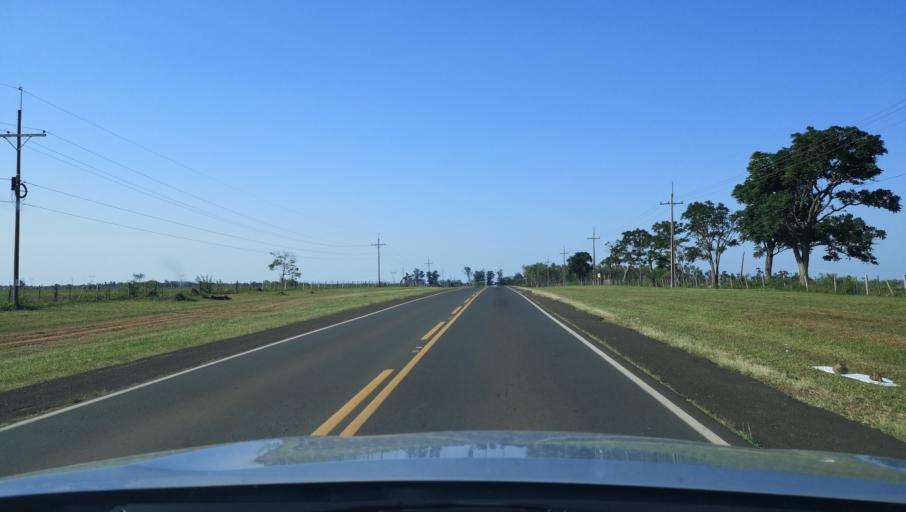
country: PY
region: Misiones
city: Santa Maria
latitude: -26.8129
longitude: -57.0228
